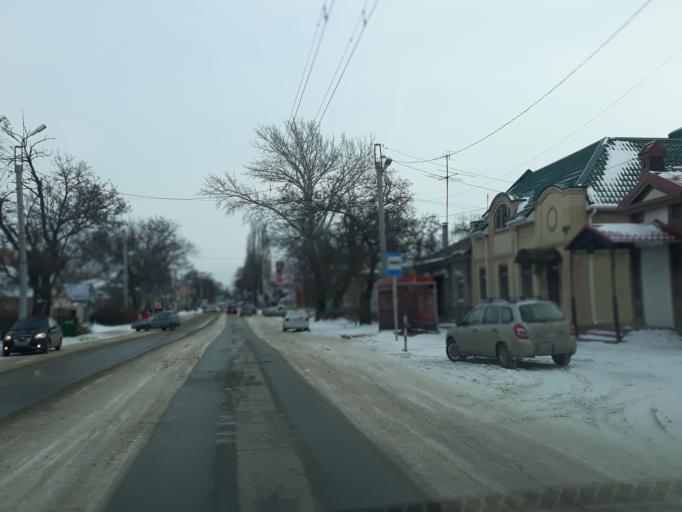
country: RU
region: Rostov
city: Taganrog
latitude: 47.2147
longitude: 38.9095
